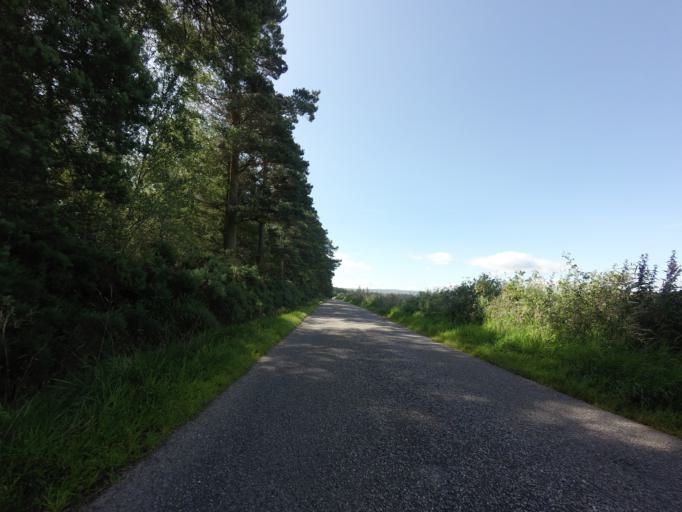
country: GB
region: Scotland
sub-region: Highland
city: Nairn
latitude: 57.5246
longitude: -3.8639
